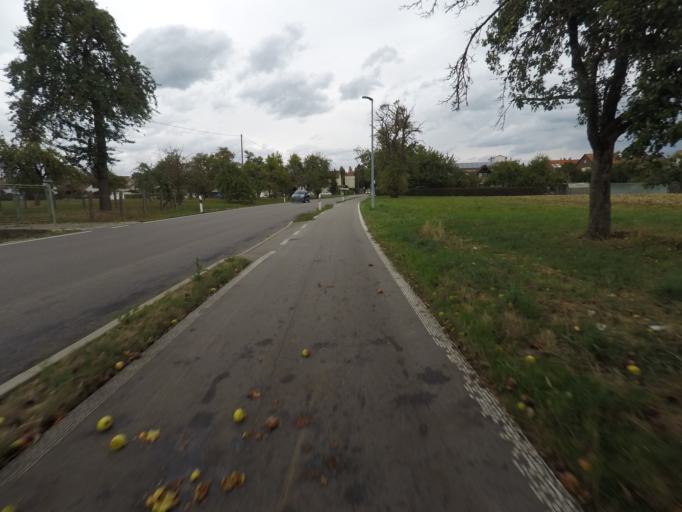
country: DE
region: Baden-Wuerttemberg
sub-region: Regierungsbezirk Stuttgart
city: Leinfelden-Echterdingen
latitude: 48.6810
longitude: 9.1672
